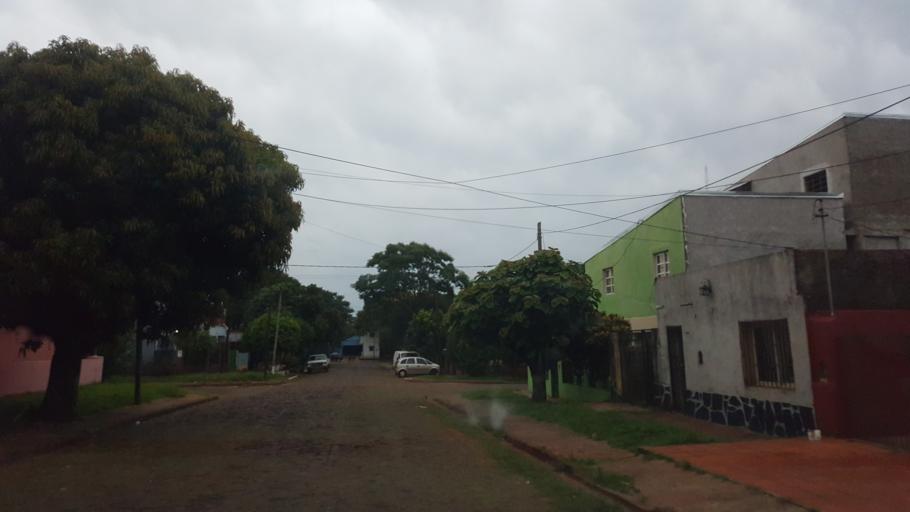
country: AR
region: Misiones
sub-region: Departamento de Capital
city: Posadas
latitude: -27.3662
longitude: -55.9297
